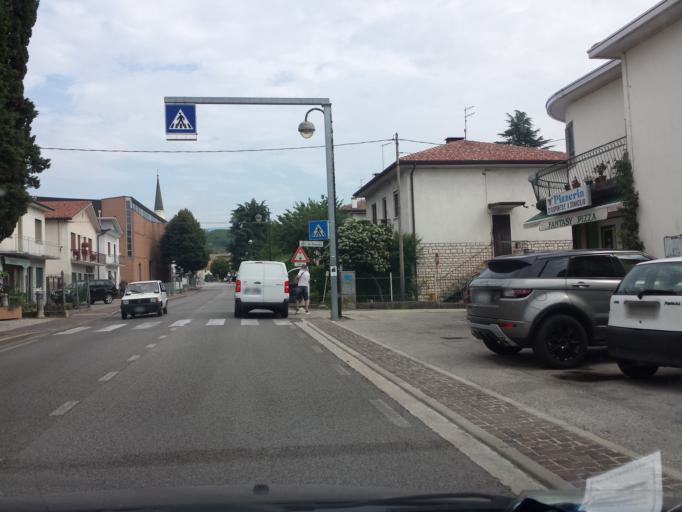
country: IT
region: Veneto
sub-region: Provincia di Vicenza
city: Breganze
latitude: 45.7045
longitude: 11.5649
